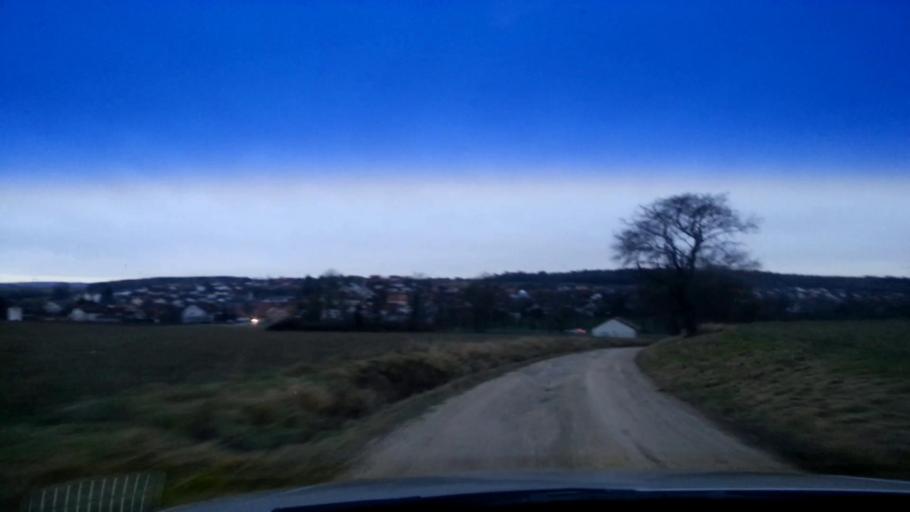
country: DE
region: Bavaria
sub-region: Upper Franconia
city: Litzendorf
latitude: 49.9161
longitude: 10.9908
